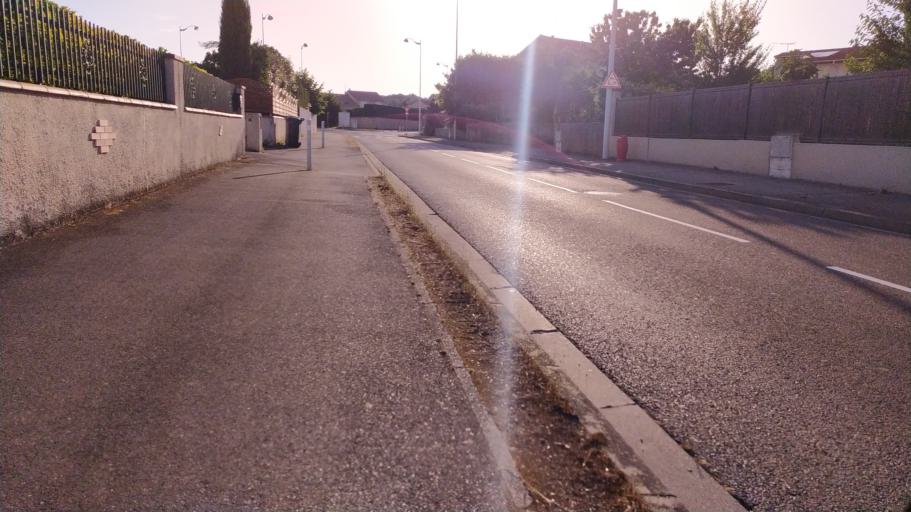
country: FR
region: Midi-Pyrenees
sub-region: Departement de la Haute-Garonne
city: Tournefeuille
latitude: 43.5838
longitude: 1.3286
